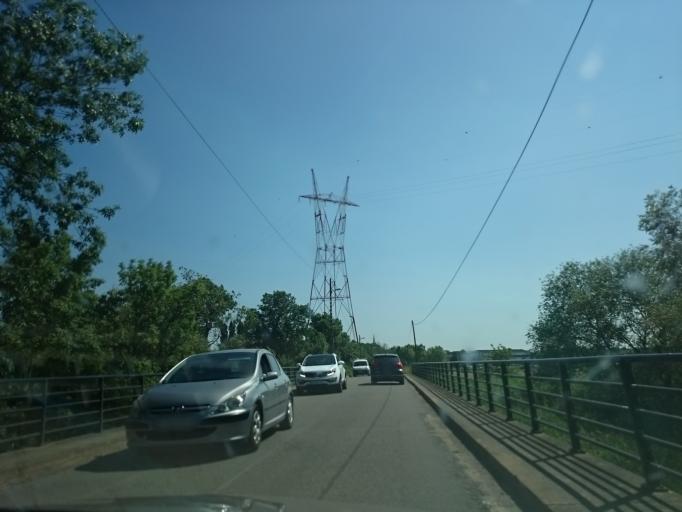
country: FR
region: Pays de la Loire
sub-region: Departement de la Loire-Atlantique
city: Le Pellerin
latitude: 47.2089
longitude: -1.7490
